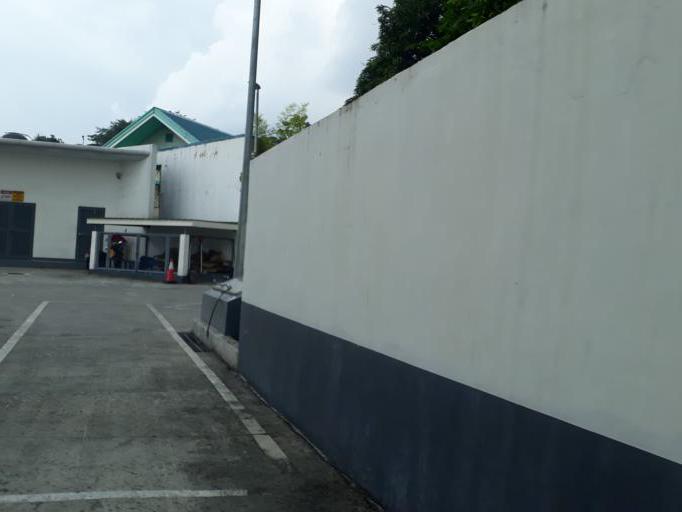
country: PH
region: Calabarzon
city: Bagong Pagasa
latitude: 14.6736
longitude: 121.0526
